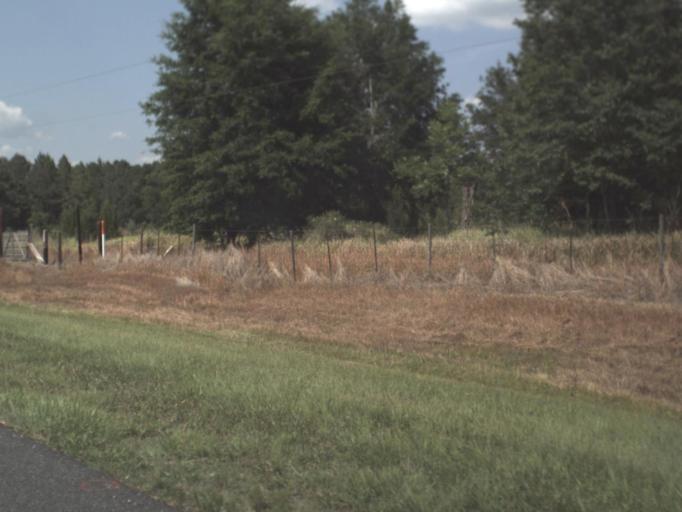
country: US
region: Florida
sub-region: Alachua County
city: Waldo
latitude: 29.7284
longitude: -82.1410
